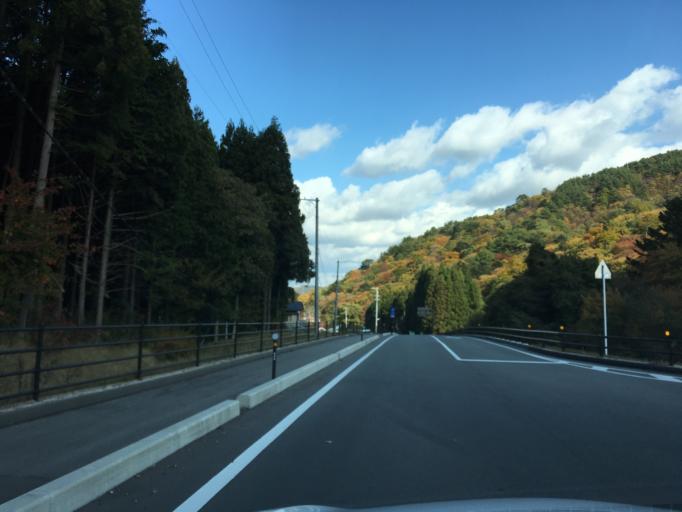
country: JP
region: Fukushima
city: Funehikimachi-funehiki
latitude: 37.2943
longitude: 140.7580
